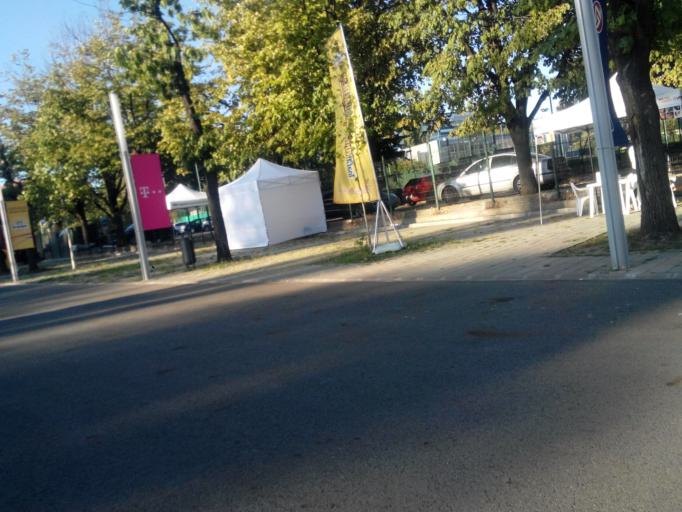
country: RO
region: Ilfov
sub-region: Comuna Fundeni-Dobroesti
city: Fundeni
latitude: 44.4389
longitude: 26.1512
